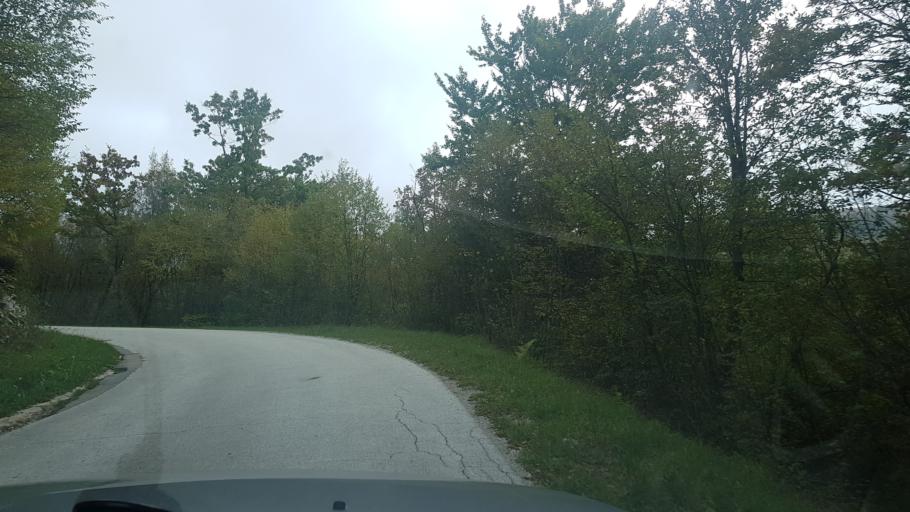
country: HR
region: Istarska
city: Buzet
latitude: 45.5086
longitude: 13.9698
